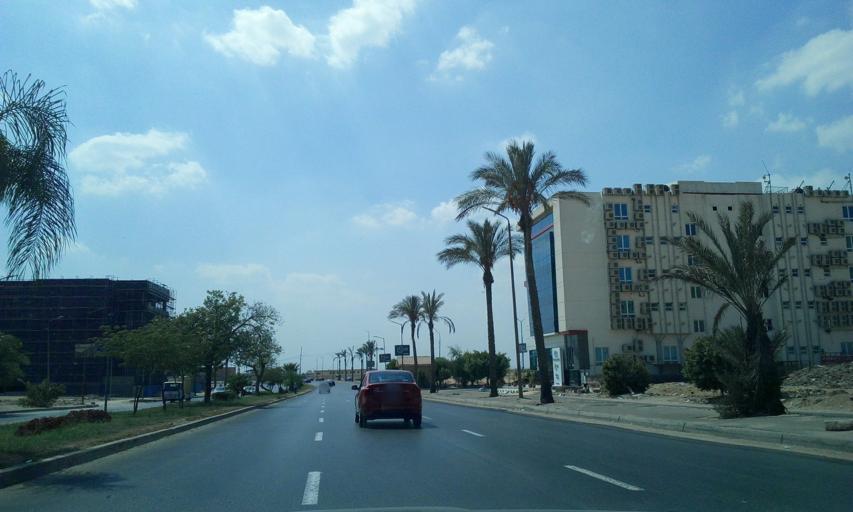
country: EG
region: Muhafazat al Qalyubiyah
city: Al Khankah
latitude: 30.0912
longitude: 31.3736
